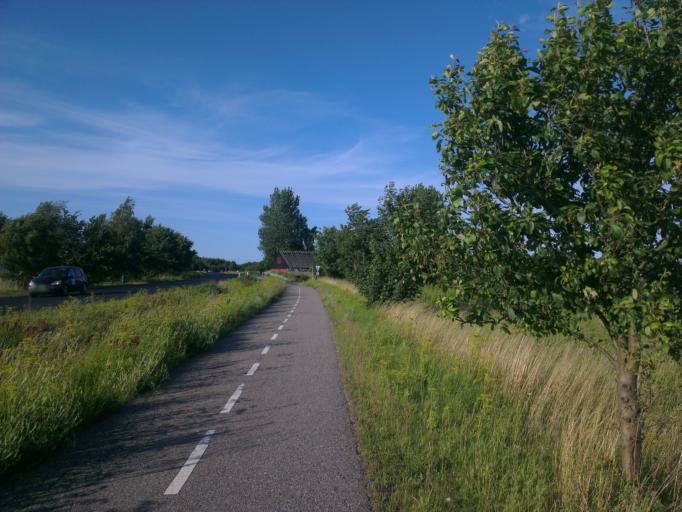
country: DK
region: Capital Region
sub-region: Frederikssund Kommune
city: Jaegerspris
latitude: 55.8118
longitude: 11.9936
